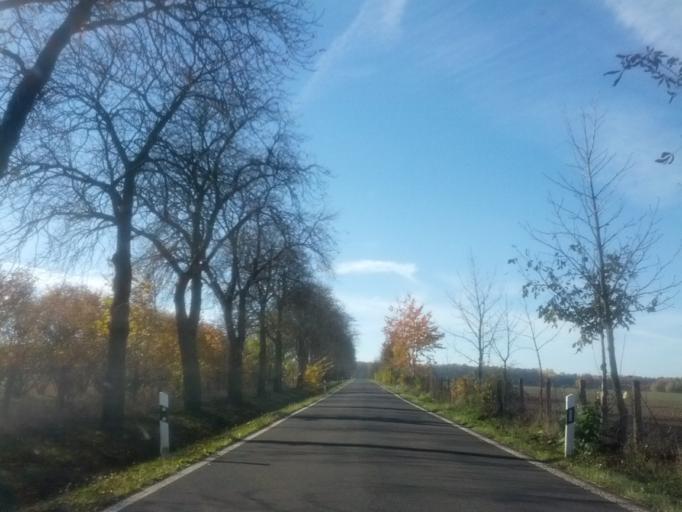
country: DE
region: Thuringia
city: Friedrichswerth
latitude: 50.9654
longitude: 10.5585
